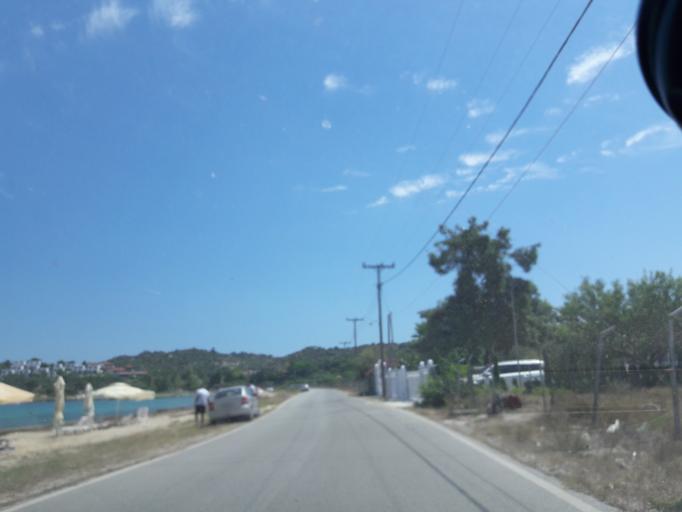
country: GR
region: Central Macedonia
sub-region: Nomos Chalkidikis
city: Ouranoupolis
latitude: 40.3184
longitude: 23.9232
